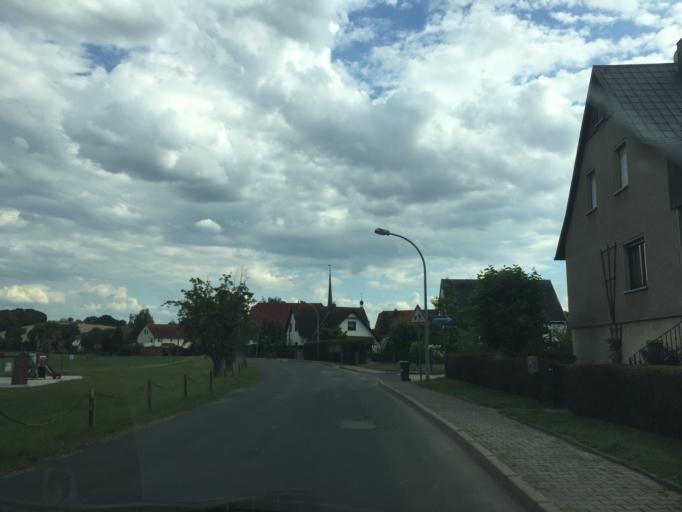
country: DE
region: Thuringia
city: Saara
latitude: 50.9545
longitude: 12.4301
